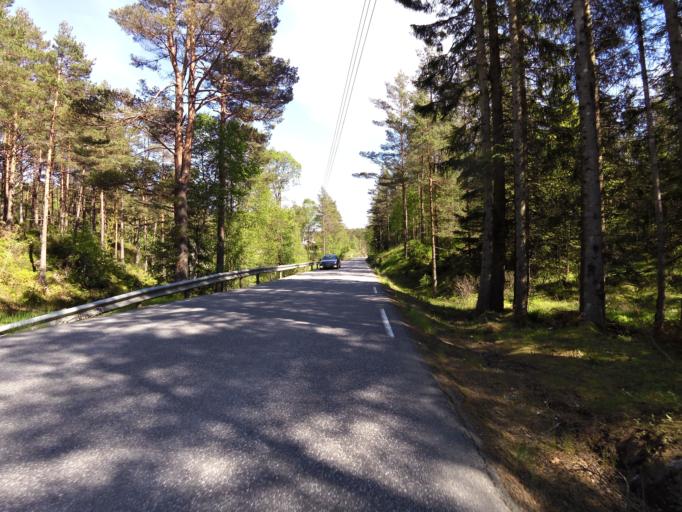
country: NO
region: Hordaland
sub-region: Stord
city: Sagvag
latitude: 59.7885
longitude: 5.4436
